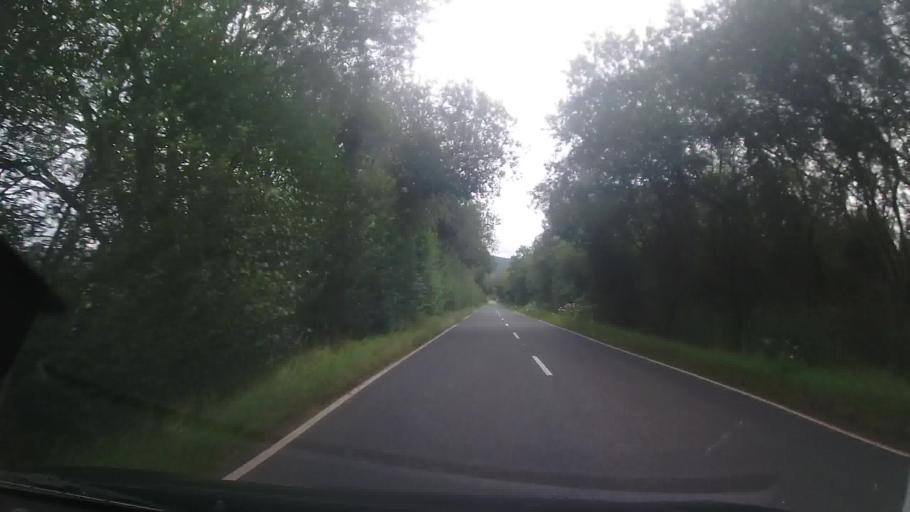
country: GB
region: Wales
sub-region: County of Ceredigion
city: Bow Street
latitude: 52.5137
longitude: -4.0064
